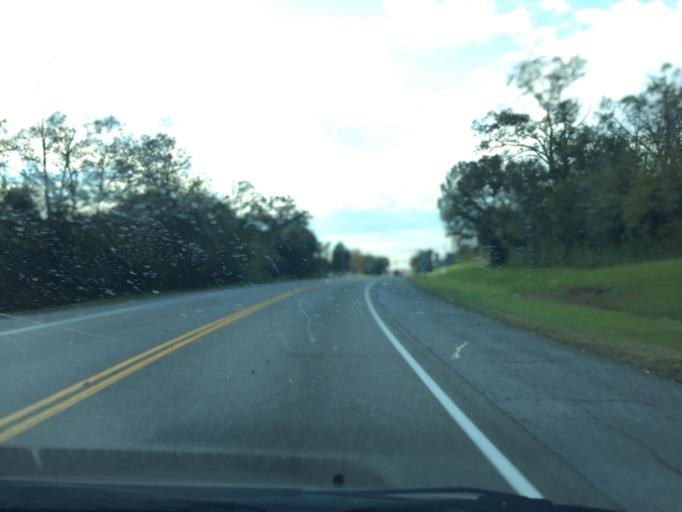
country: US
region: Tennessee
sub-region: Loudon County
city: Loudon
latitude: 35.7180
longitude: -84.3552
